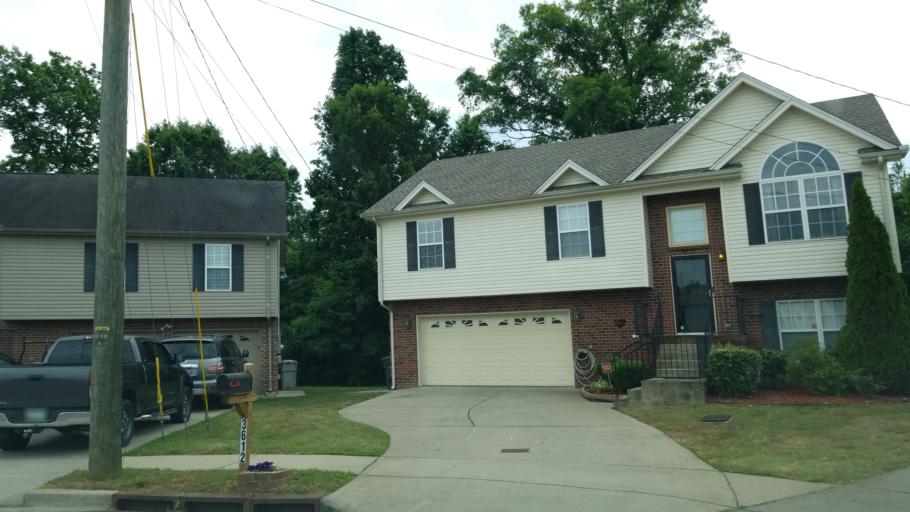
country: US
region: Tennessee
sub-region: Rutherford County
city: La Vergne
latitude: 36.0593
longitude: -86.5875
